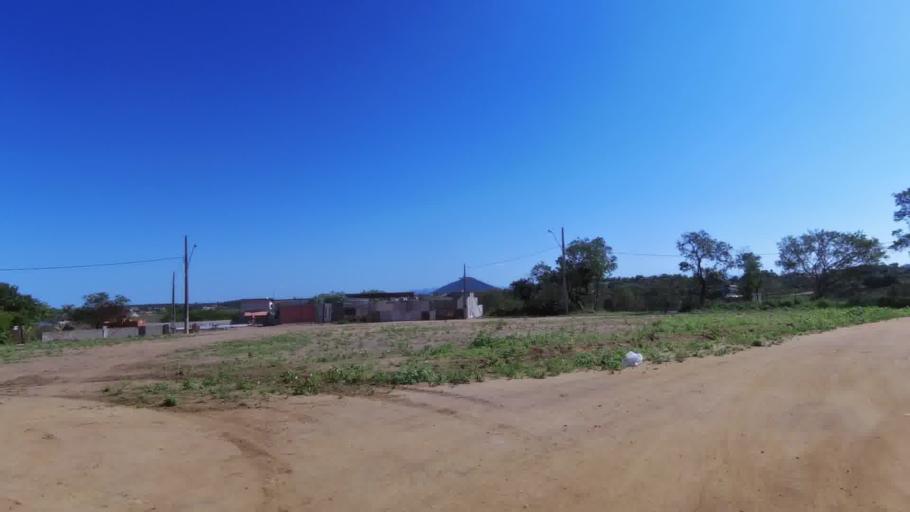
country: BR
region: Espirito Santo
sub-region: Guarapari
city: Guarapari
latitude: -20.7378
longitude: -40.5465
